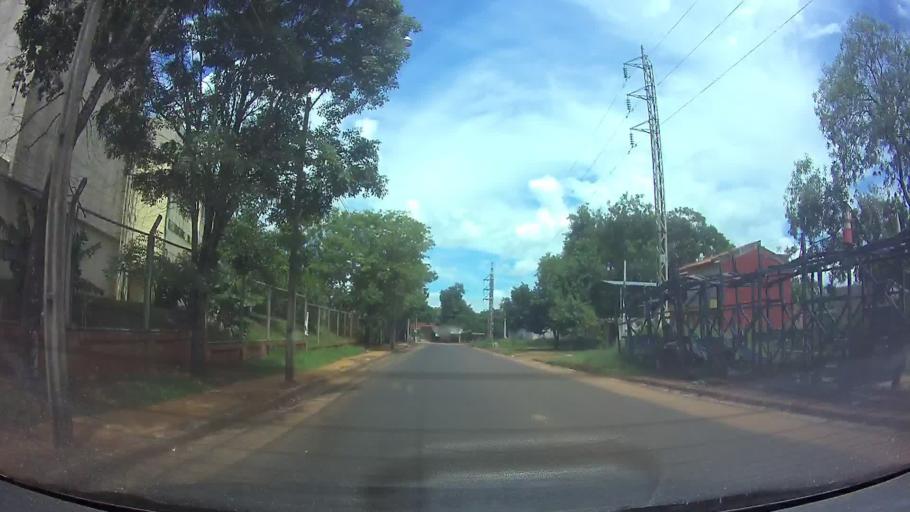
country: PY
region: Central
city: San Lorenzo
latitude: -25.3226
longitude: -57.5099
